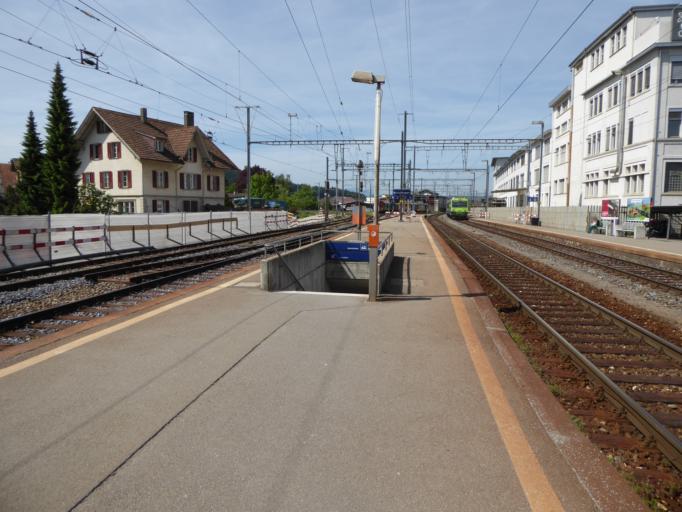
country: CH
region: Bern
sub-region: Bern-Mittelland District
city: Konolfingen
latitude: 46.8804
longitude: 7.6212
